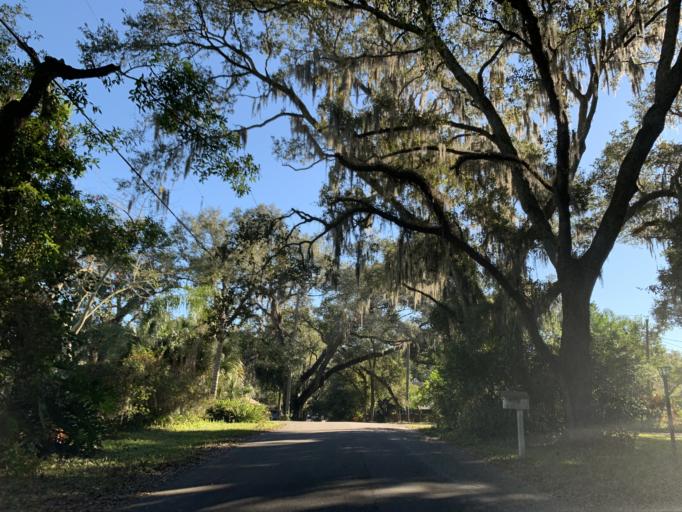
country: US
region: Florida
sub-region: Hillsborough County
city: Temple Terrace
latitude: 28.0276
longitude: -82.4283
